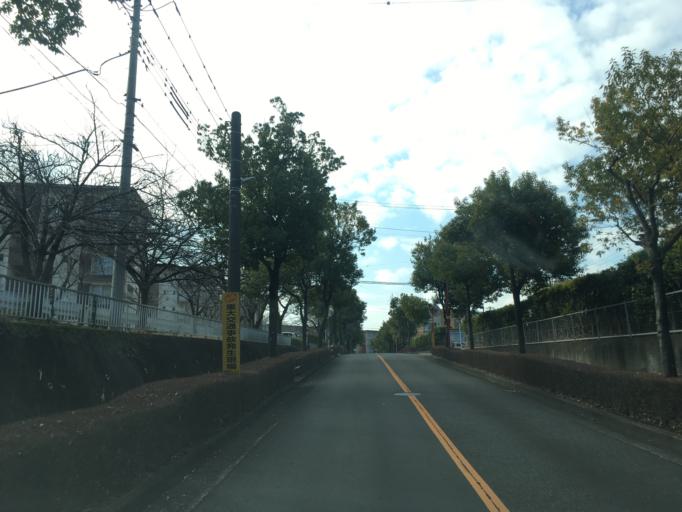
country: JP
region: Tokyo
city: Hino
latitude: 35.6206
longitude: 139.4353
